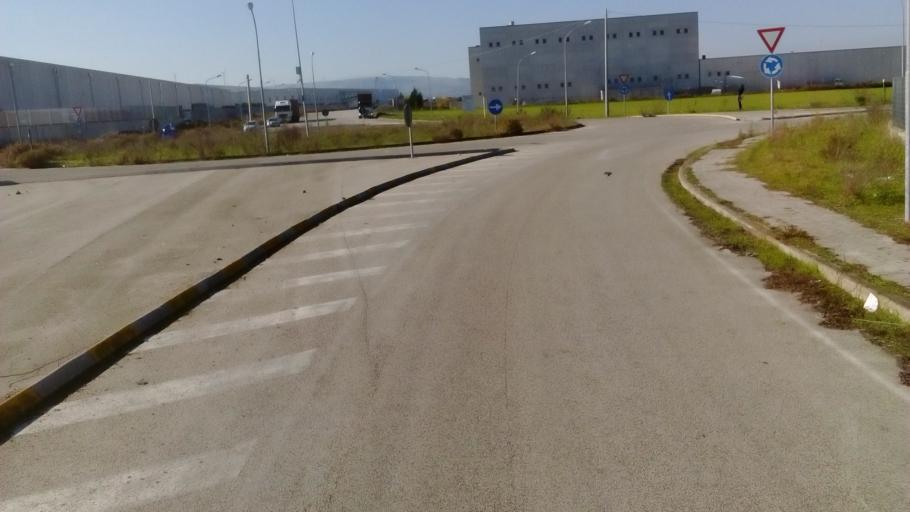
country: IT
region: Basilicate
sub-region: Provincia di Potenza
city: Melfi
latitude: 41.0782
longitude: 15.6599
